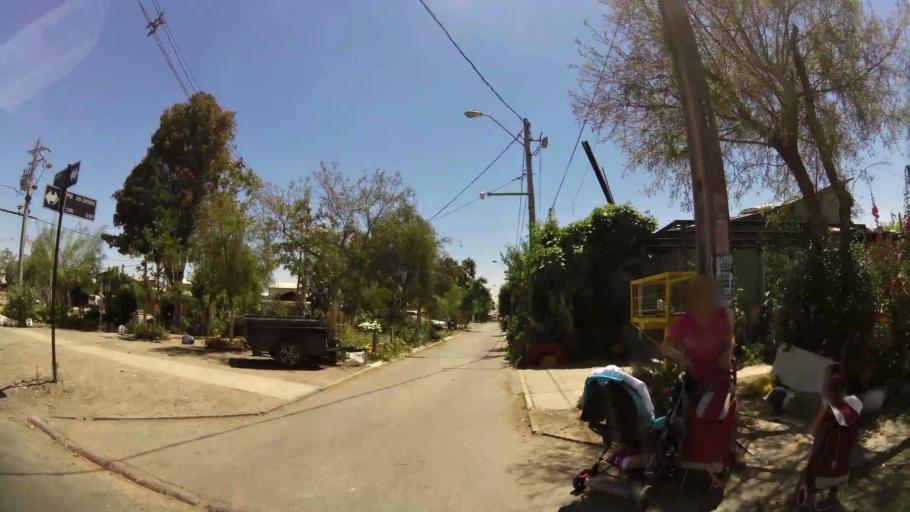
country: CL
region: Santiago Metropolitan
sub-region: Provincia de Santiago
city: La Pintana
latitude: -33.5670
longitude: -70.6593
